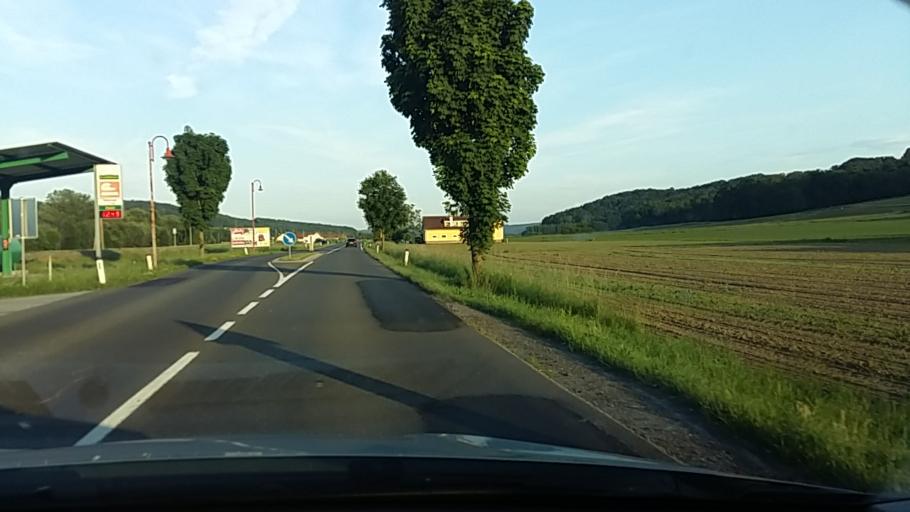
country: AT
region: Styria
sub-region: Politischer Bezirk Suedoststeiermark
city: Hatzendorf
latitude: 46.9771
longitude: 16.0042
